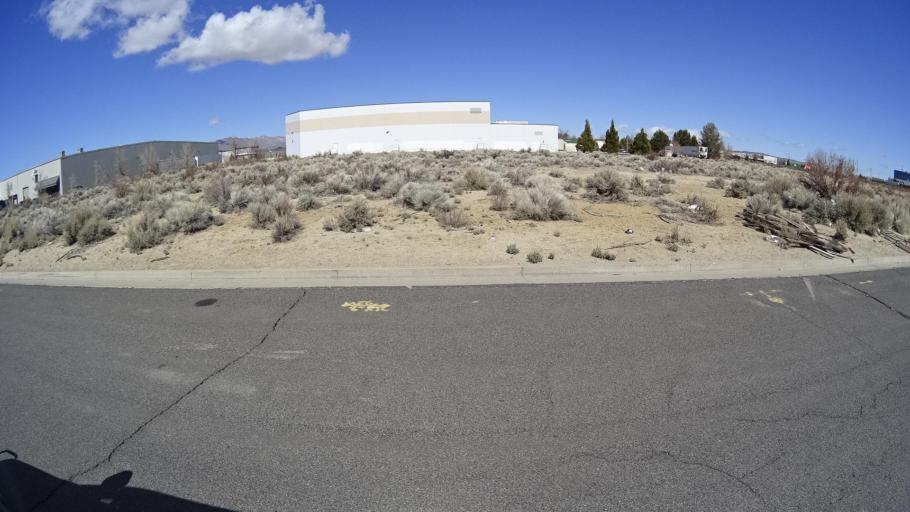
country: US
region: Nevada
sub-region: Washoe County
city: Lemmon Valley
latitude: 39.6399
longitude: -119.8932
